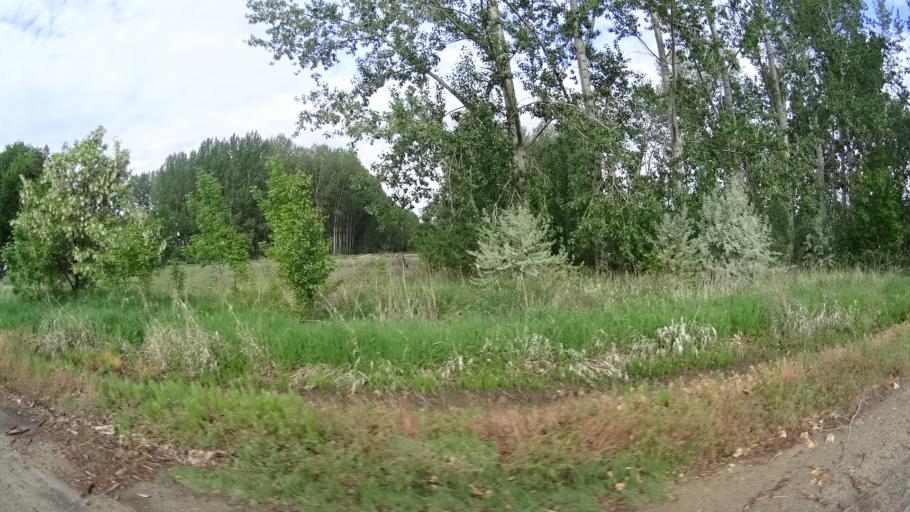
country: US
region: Idaho
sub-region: Ada County
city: Star
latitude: 43.6987
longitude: -116.5128
